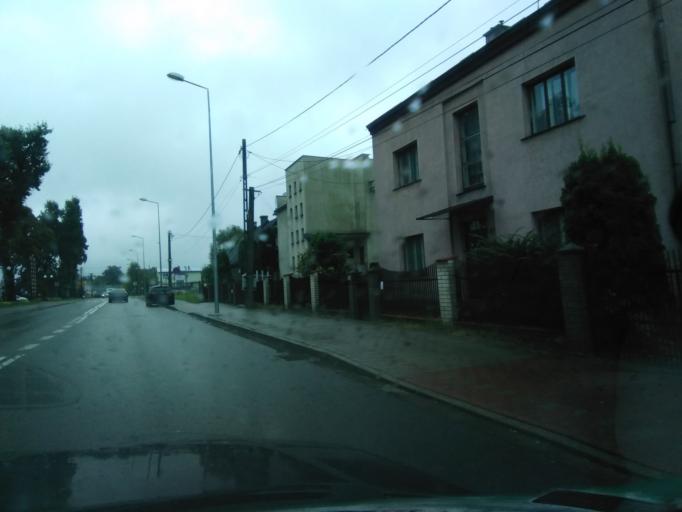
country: PL
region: Subcarpathian Voivodeship
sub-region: Powiat debicki
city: Debica
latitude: 50.0589
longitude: 21.4074
